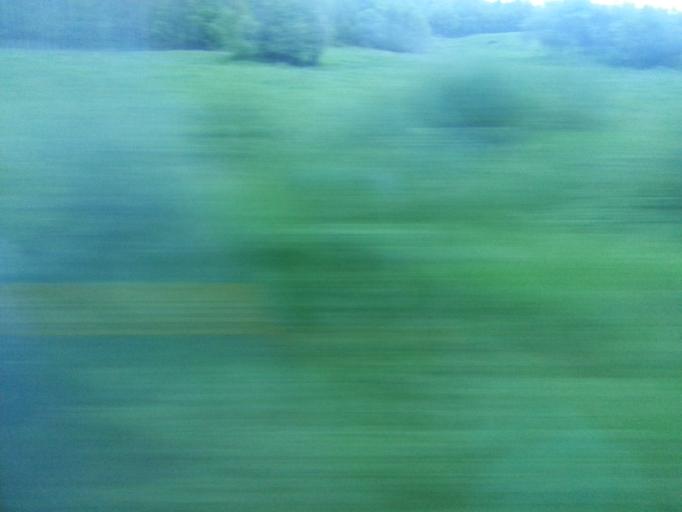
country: NO
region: Oppland
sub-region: Dovre
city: Dombas
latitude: 62.0553
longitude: 9.1367
